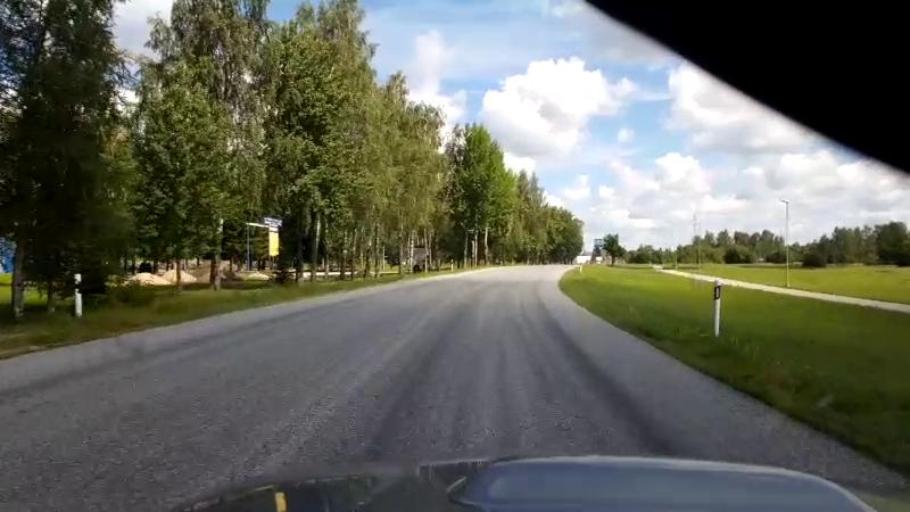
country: EE
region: Laeaene-Virumaa
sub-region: Tapa vald
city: Tapa
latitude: 59.2532
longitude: 25.9396
